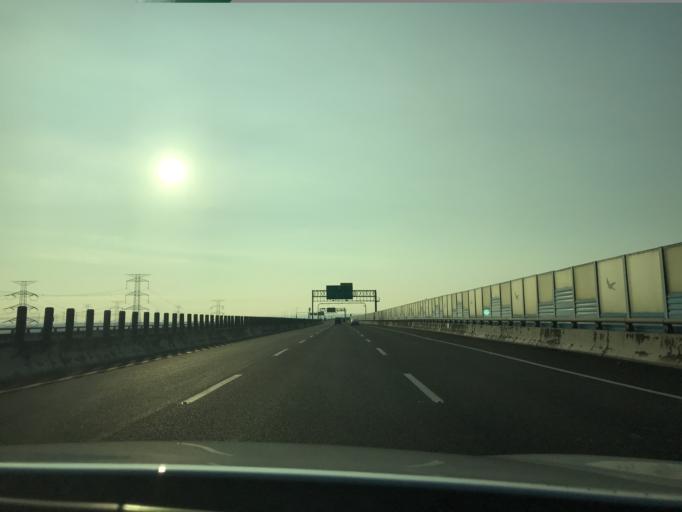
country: TW
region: Taiwan
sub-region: Changhua
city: Chang-hua
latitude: 24.1159
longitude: 120.5402
